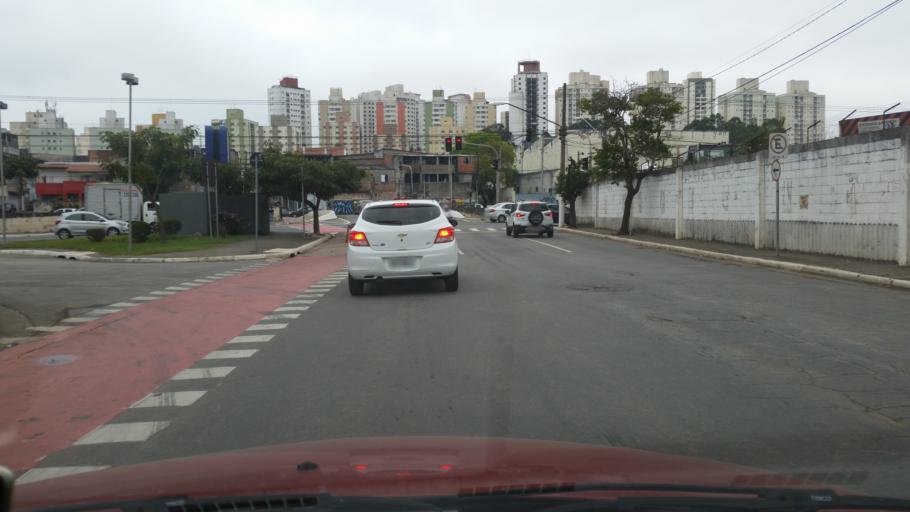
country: BR
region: Sao Paulo
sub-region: Sao Caetano Do Sul
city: Sao Caetano do Sul
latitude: -23.5957
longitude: -46.5832
